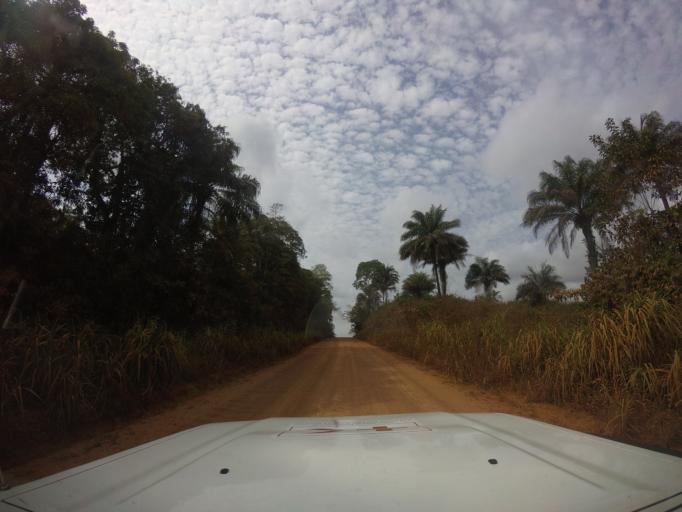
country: LR
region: Grand Cape Mount
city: Robertsport
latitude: 6.7129
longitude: -11.0861
